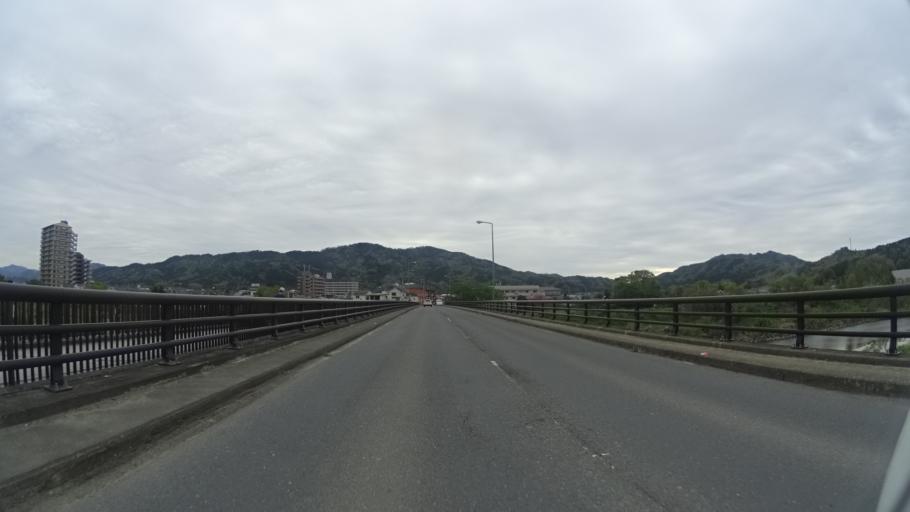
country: JP
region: Kyoto
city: Kameoka
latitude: 35.0513
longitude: 135.5508
